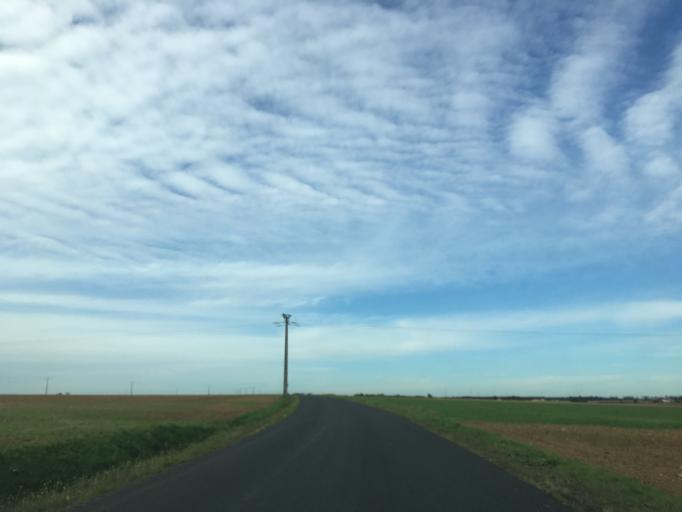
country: FR
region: Poitou-Charentes
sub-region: Departement des Deux-Sevres
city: Beauvoir-sur-Niort
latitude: 46.0708
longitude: -0.4870
